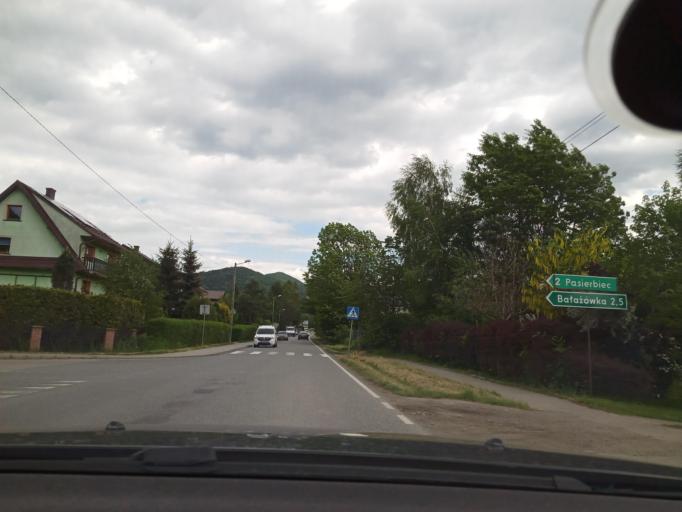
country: PL
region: Lesser Poland Voivodeship
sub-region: Powiat limanowski
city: Limanowa
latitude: 49.7405
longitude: 20.3830
